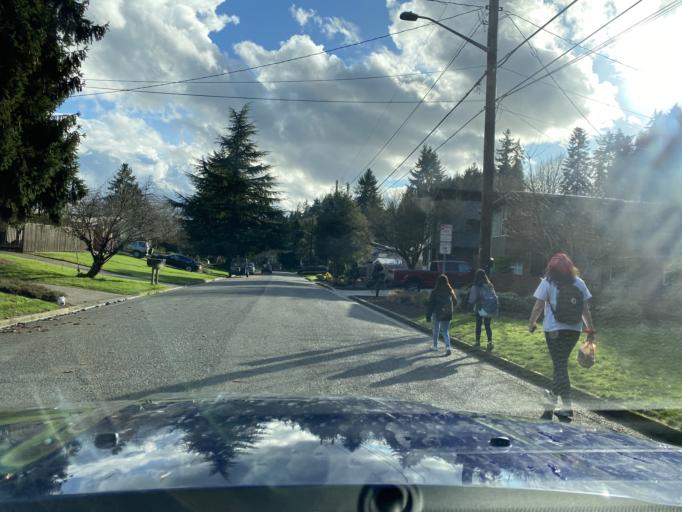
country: US
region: Washington
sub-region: King County
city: Bellevue
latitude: 47.6078
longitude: -122.1951
